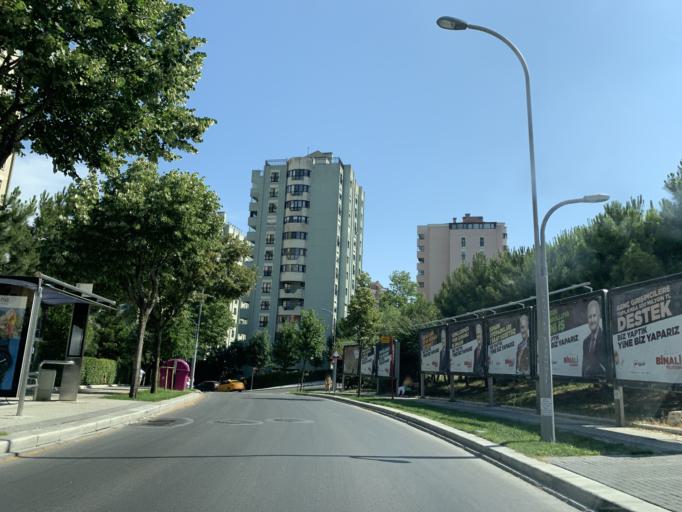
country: TR
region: Istanbul
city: Esenyurt
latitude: 41.0677
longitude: 28.6775
